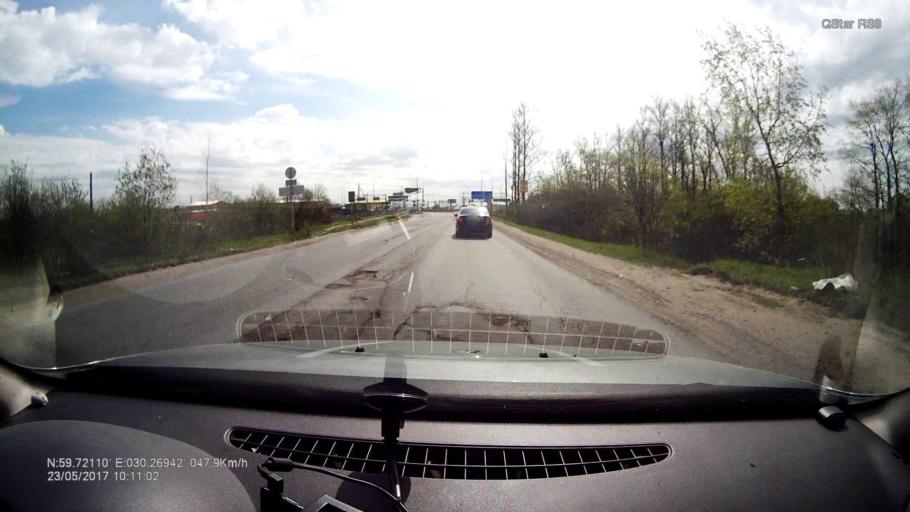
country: RU
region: St.-Petersburg
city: Aleksandrovskaya
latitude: 59.7211
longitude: 30.2695
